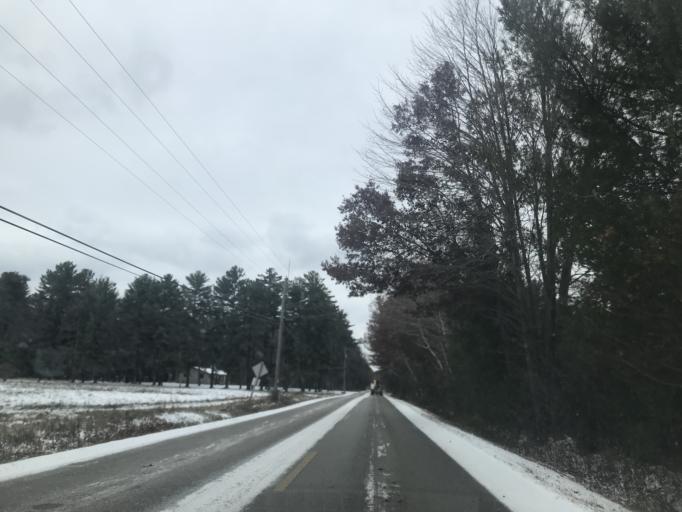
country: US
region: Wisconsin
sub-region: Marinette County
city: Marinette
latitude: 45.0689
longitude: -87.6595
